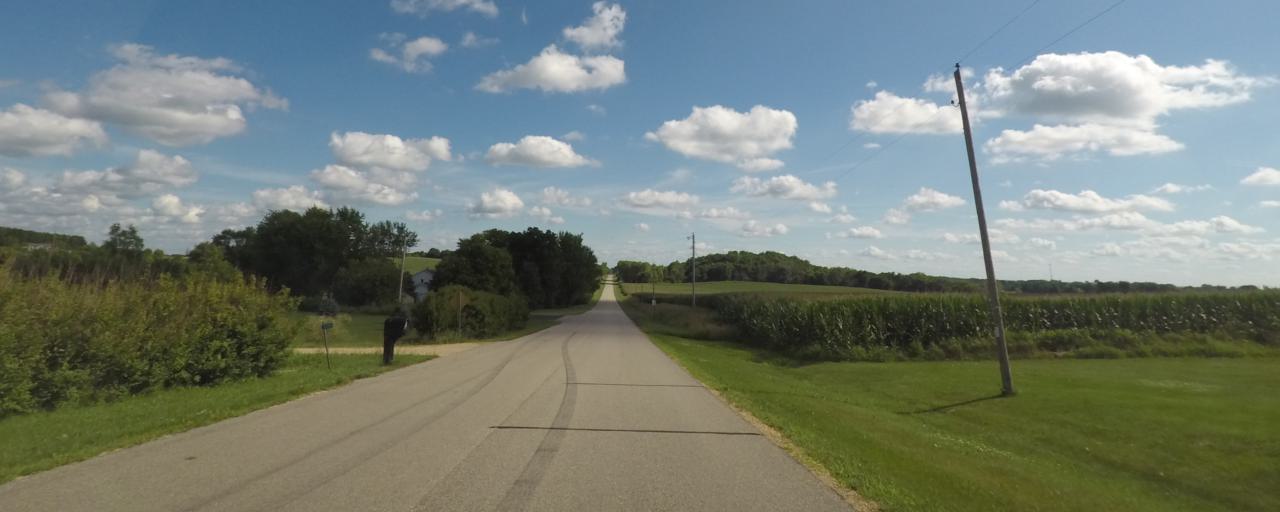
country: US
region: Wisconsin
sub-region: Dane County
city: Stoughton
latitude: 42.9104
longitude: -89.1319
